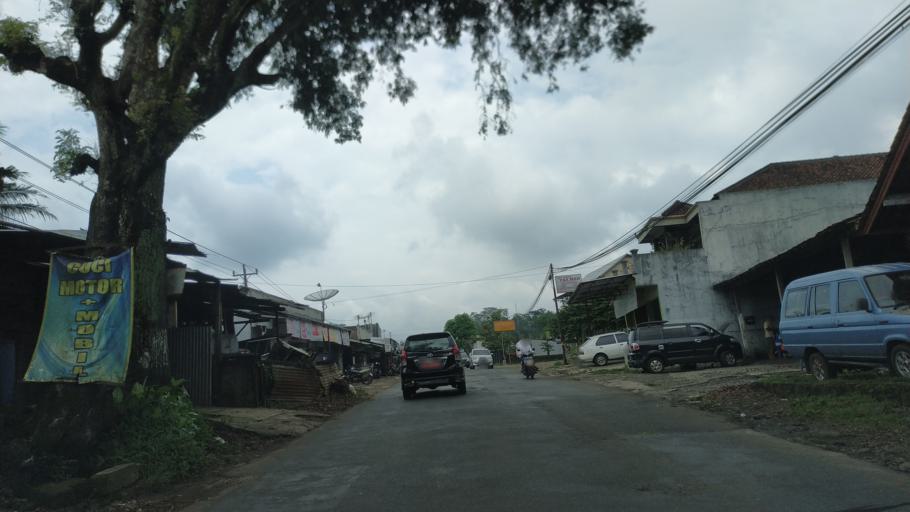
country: ID
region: Central Java
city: Weleri
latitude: -7.0941
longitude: 110.0558
